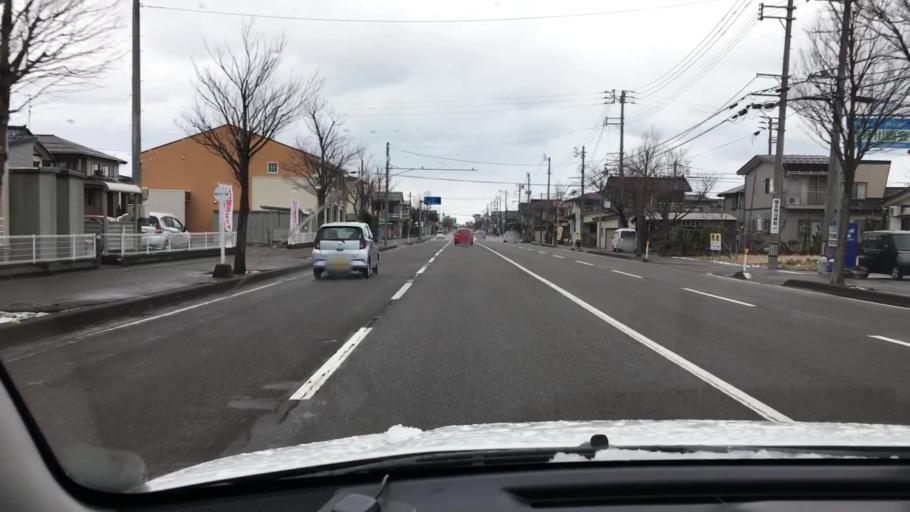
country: JP
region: Niigata
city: Joetsu
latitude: 37.1420
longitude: 138.2287
